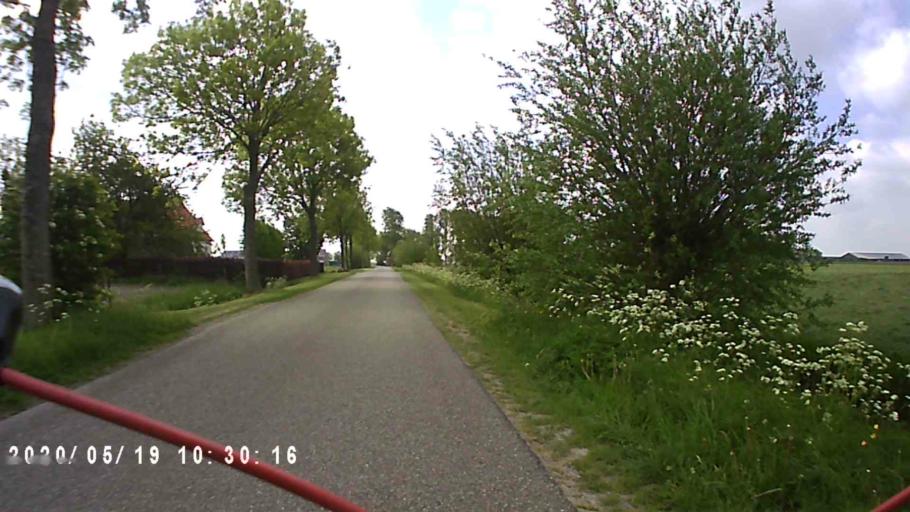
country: NL
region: Friesland
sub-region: Gemeente Kollumerland en Nieuwkruisland
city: Kollum
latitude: 53.2951
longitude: 6.1958
